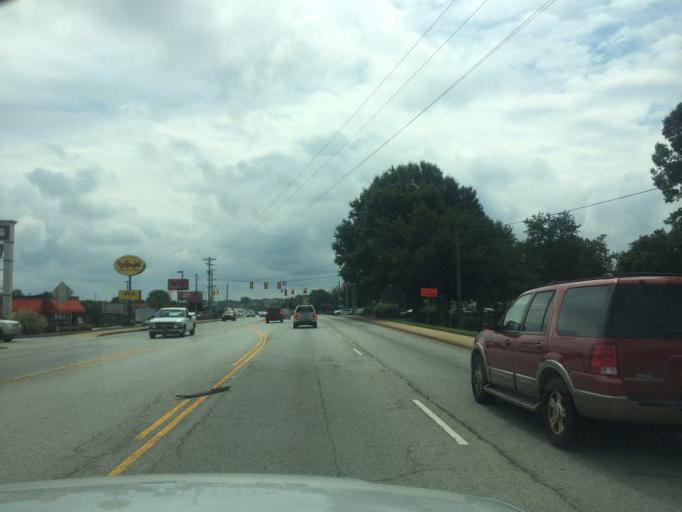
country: US
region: South Carolina
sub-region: Greenville County
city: Mauldin
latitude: 34.8227
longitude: -82.2889
